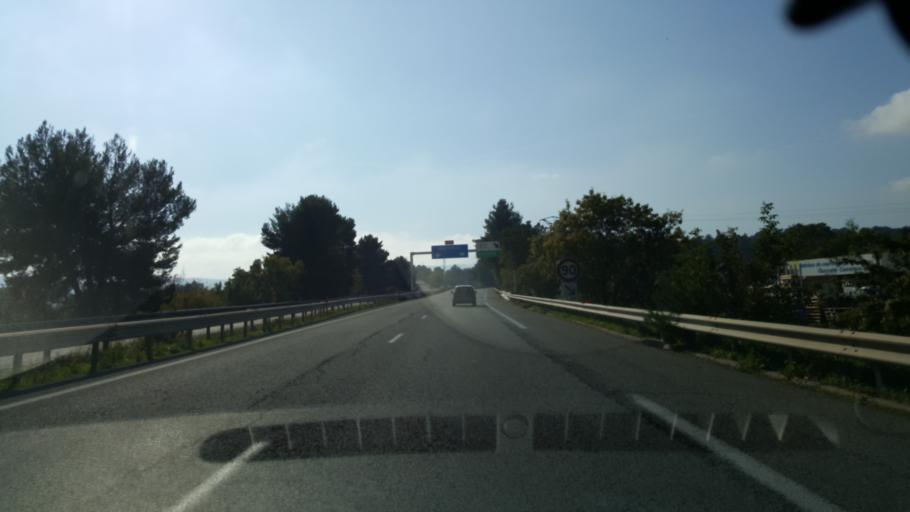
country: FR
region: Provence-Alpes-Cote d'Azur
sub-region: Departement des Bouches-du-Rhone
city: Aubagne
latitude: 43.3079
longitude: 5.5776
